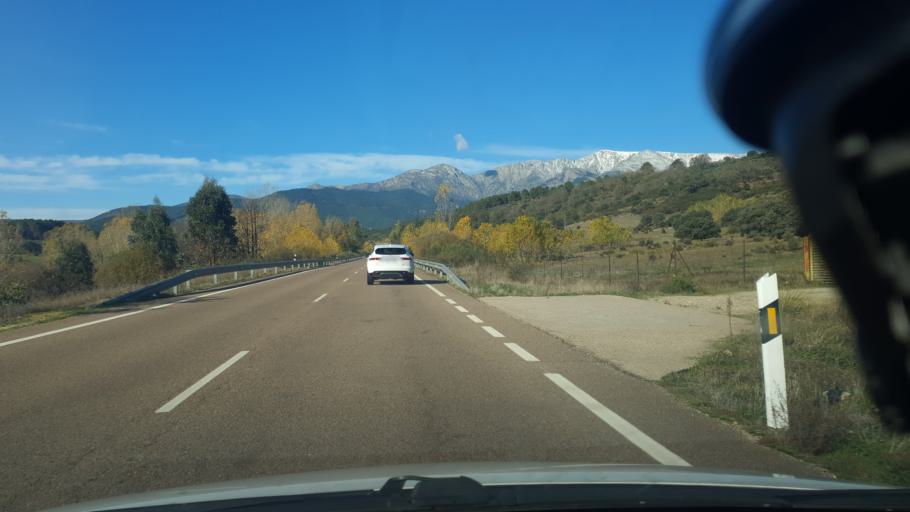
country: ES
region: Castille and Leon
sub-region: Provincia de Avila
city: Arenas de San Pedro
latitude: 40.1871
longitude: -5.0602
